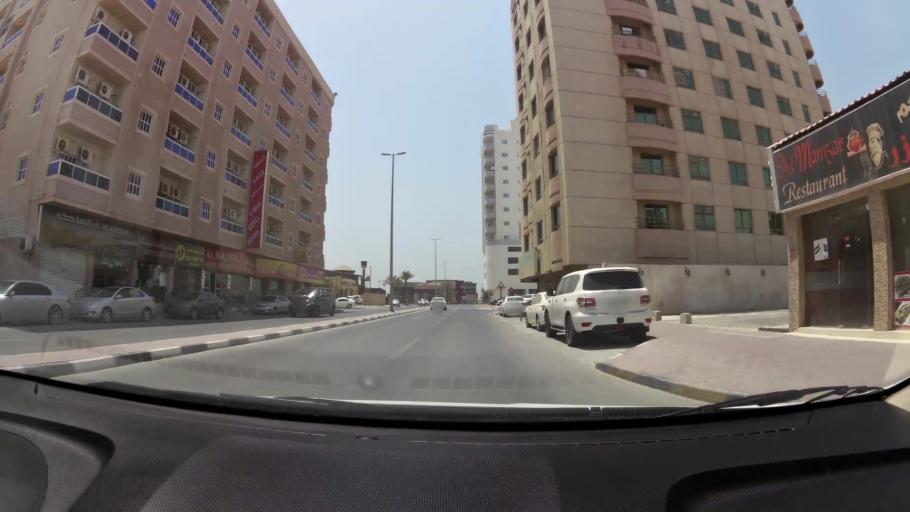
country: AE
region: Ajman
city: Ajman
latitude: 25.4062
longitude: 55.4328
